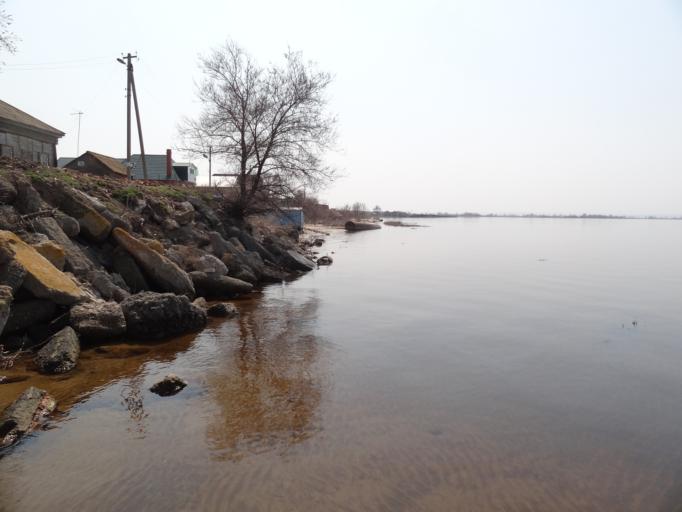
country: RU
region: Saratov
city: Privolzhskiy
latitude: 51.2512
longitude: 45.9084
